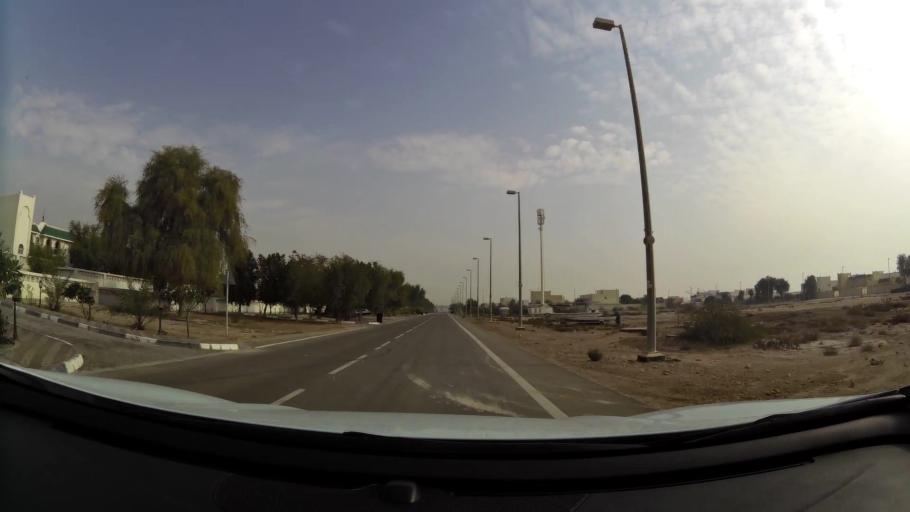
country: AE
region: Abu Dhabi
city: Abu Dhabi
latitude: 24.6654
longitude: 54.7634
